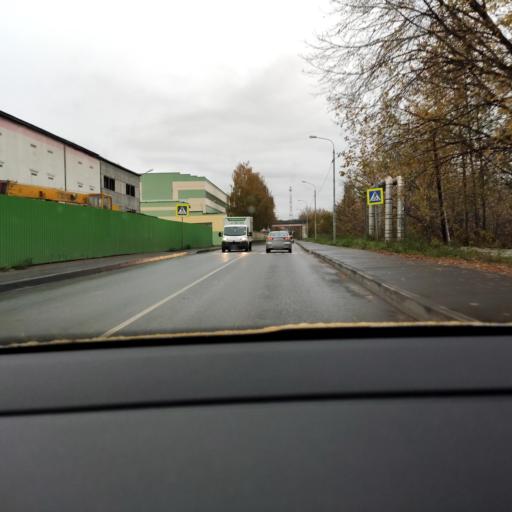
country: RU
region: Moskovskaya
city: Ivanteyevka
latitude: 55.9617
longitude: 37.9276
